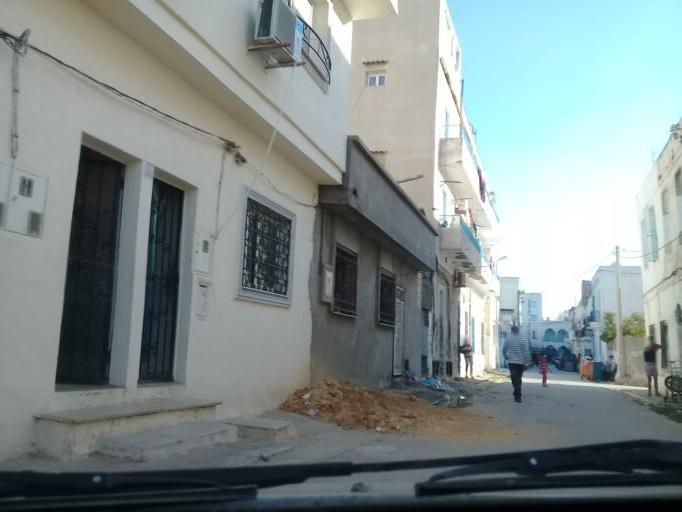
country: TN
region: Tunis
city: La Goulette
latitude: 36.8198
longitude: 10.3076
